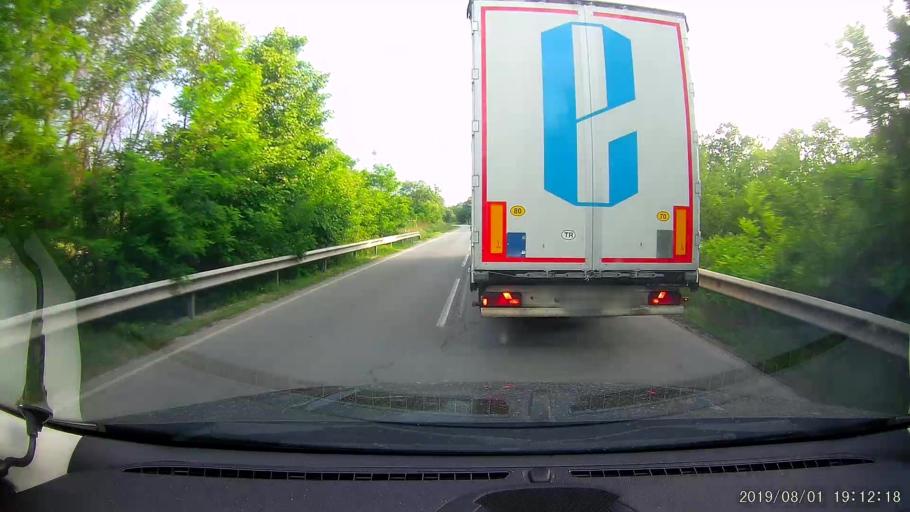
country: BG
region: Shumen
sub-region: Obshtina Smyadovo
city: Smyadovo
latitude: 42.9655
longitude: 26.9513
